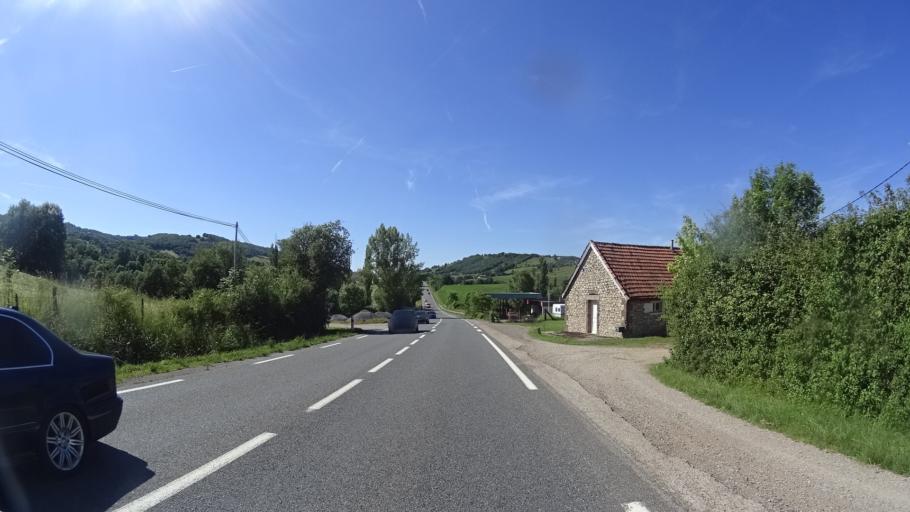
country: FR
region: Midi-Pyrenees
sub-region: Departement de l'Aveyron
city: Saint-Christophe-Vallon
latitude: 44.4743
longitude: 2.4103
